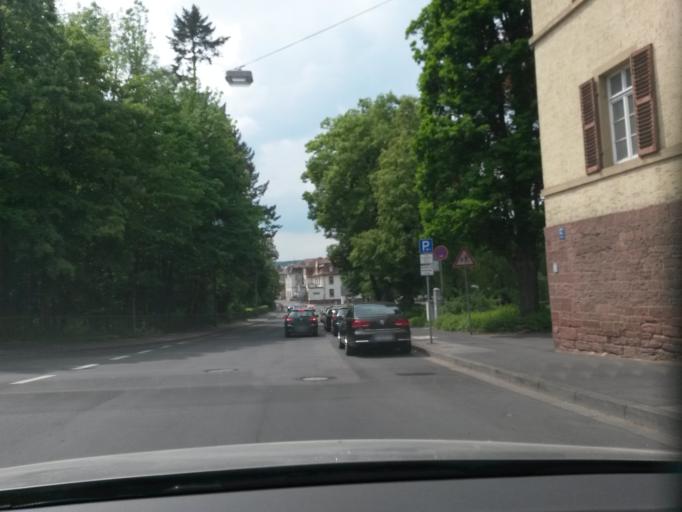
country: DE
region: Bavaria
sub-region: Regierungsbezirk Unterfranken
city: Bad Kissingen
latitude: 50.2009
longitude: 10.0832
